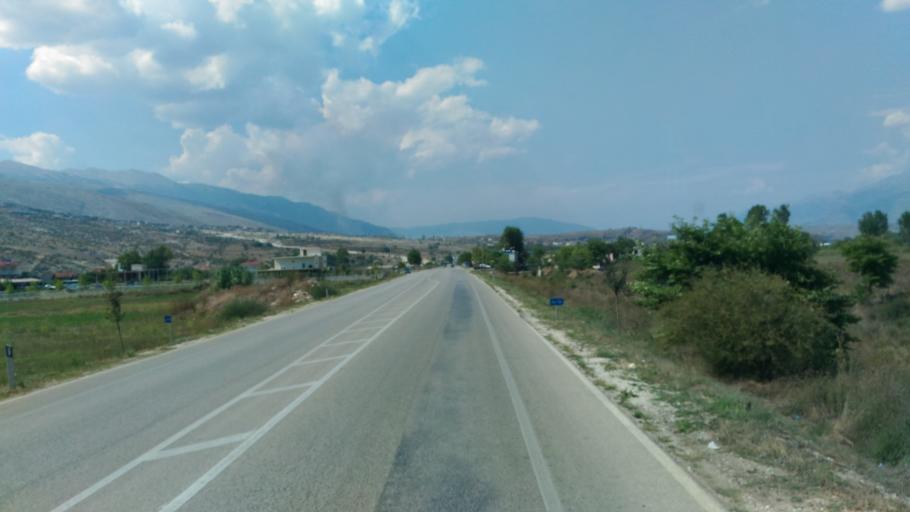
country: AL
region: Gjirokaster
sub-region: Rrethi i Gjirokastres
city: Dervician
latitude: 40.0326
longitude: 20.1832
